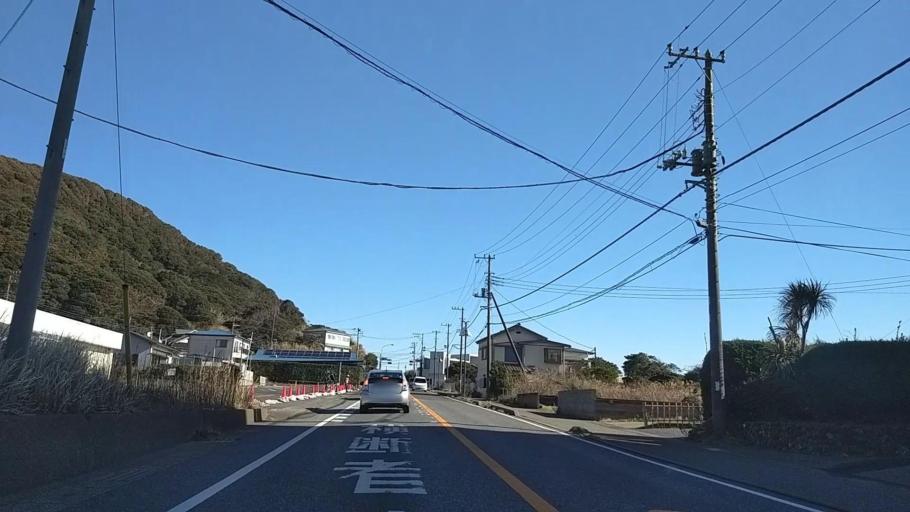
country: JP
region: Chiba
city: Kawaguchi
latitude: 35.0594
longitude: 140.0682
